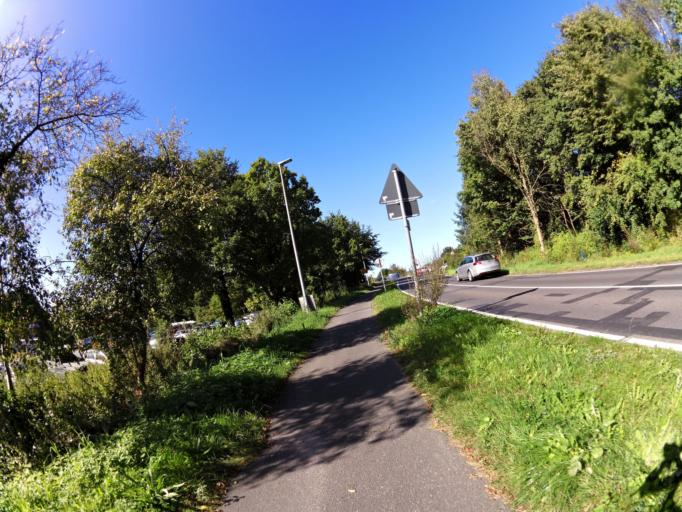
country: DE
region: Schleswig-Holstein
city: Barkelsby
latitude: 54.4877
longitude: 9.8232
